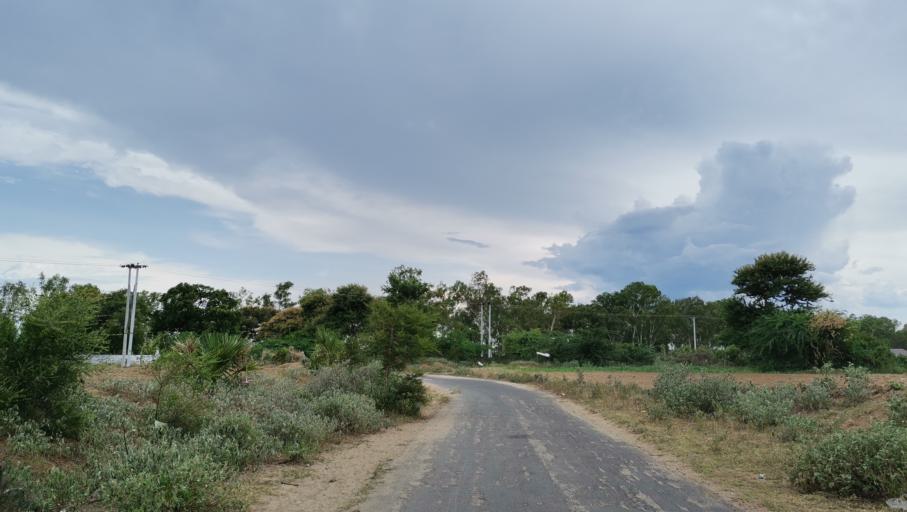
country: MM
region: Mandalay
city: Myingyan
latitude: 21.8152
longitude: 95.3967
